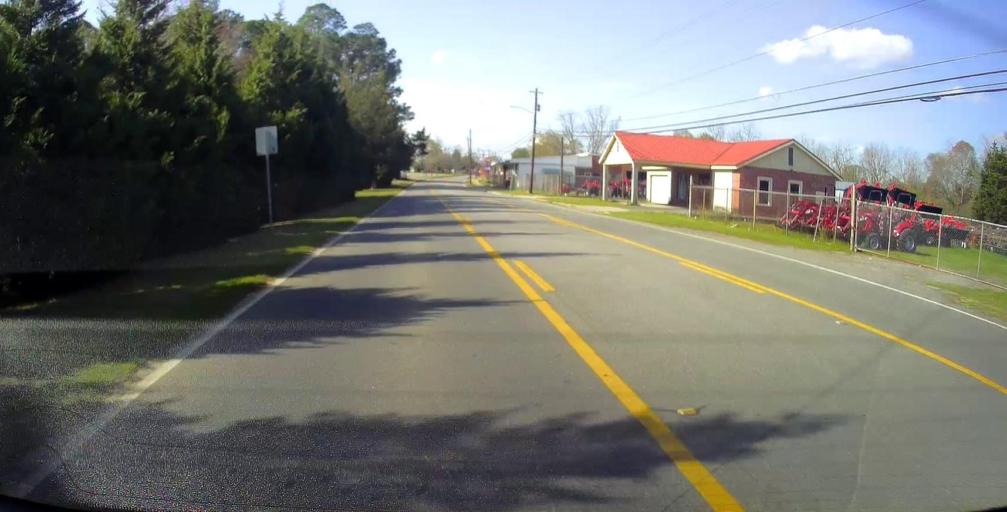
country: US
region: Georgia
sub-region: Dodge County
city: Eastman
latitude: 32.1848
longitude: -83.1704
